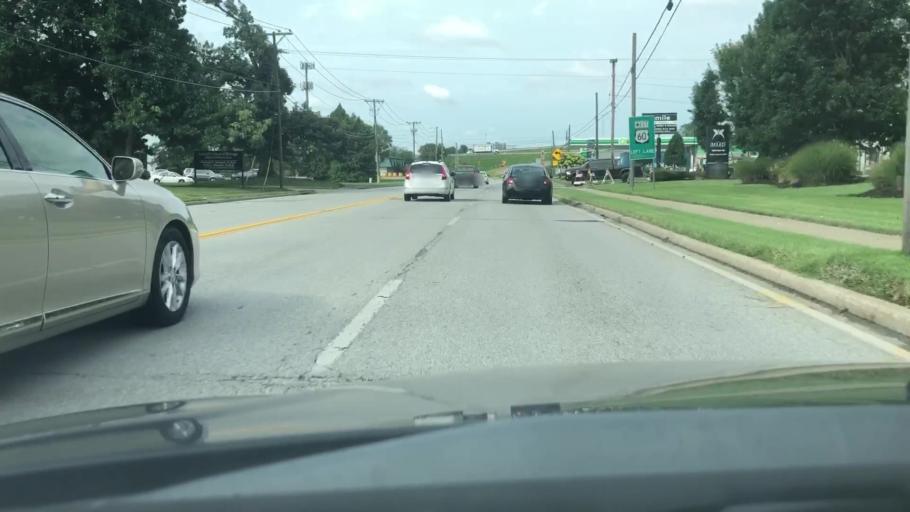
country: US
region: Kentucky
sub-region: Jefferson County
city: Lyndon
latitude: 38.2528
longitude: -85.6148
